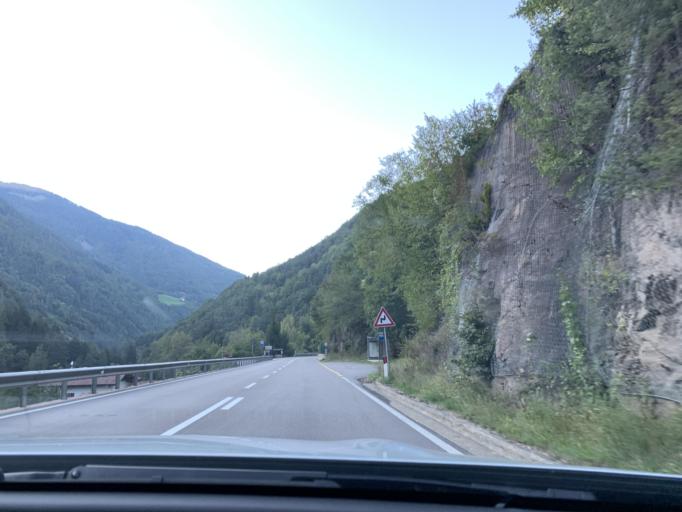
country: IT
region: Trentino-Alto Adige
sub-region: Bolzano
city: Cornedo All'Isarco
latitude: 46.4562
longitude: 11.4287
